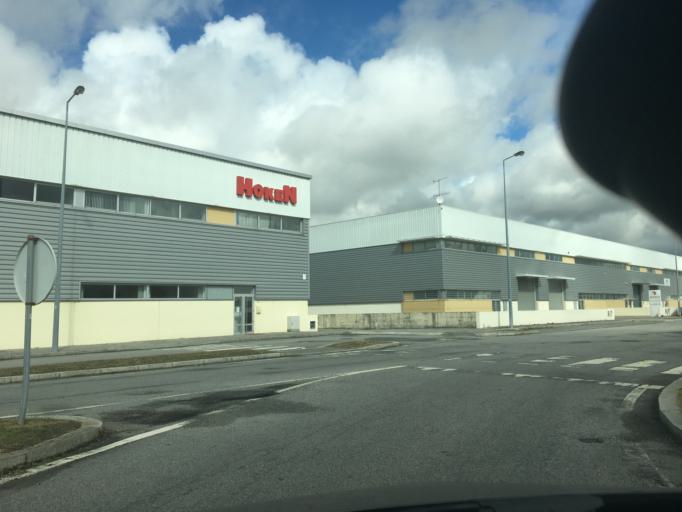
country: PT
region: Porto
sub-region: Maia
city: Gemunde
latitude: 41.2583
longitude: -8.6580
